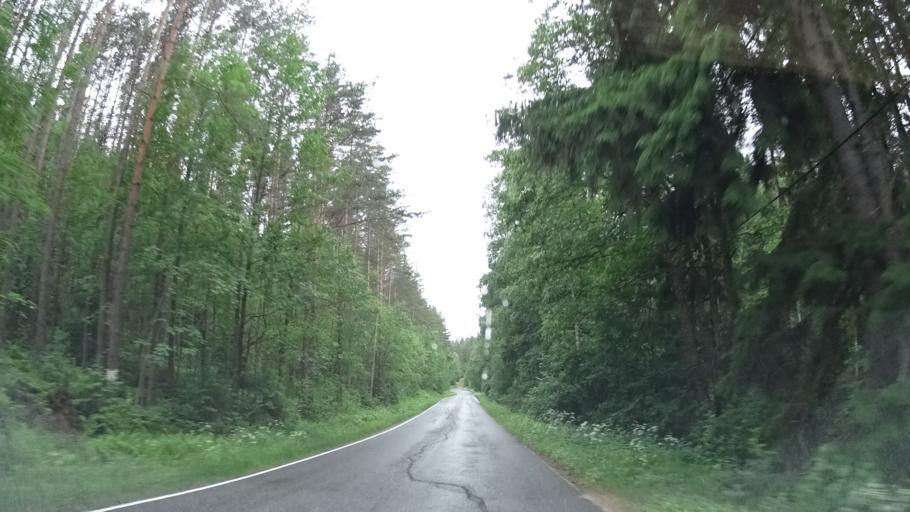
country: FI
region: Varsinais-Suomi
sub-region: Salo
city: Saerkisalo
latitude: 60.2562
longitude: 22.9779
